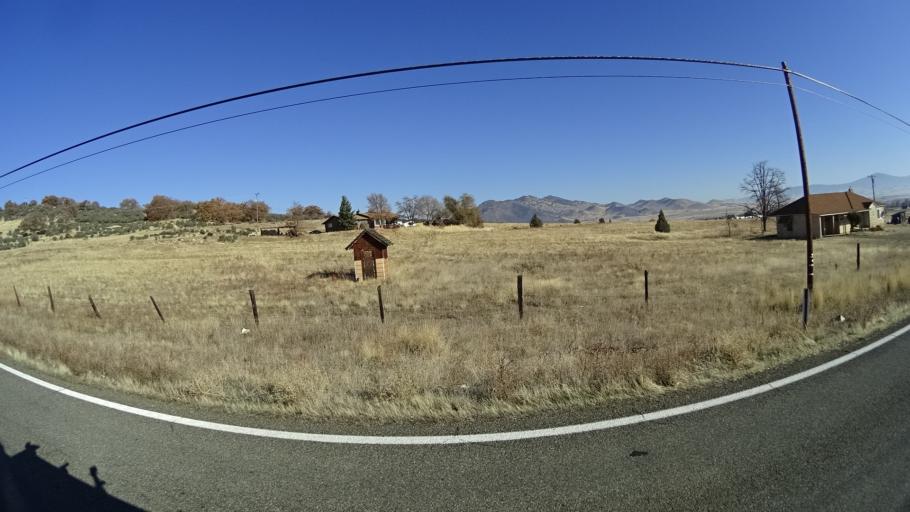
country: US
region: California
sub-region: Siskiyou County
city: Yreka
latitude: 41.7373
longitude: -122.6019
